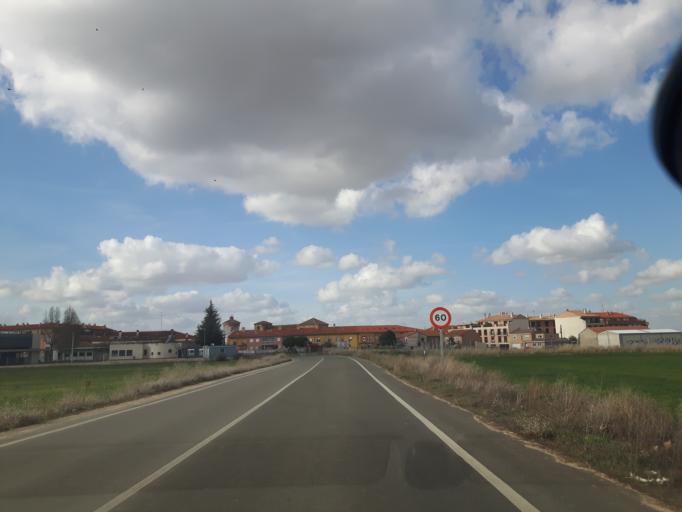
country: ES
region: Castille and Leon
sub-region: Provincia de Salamanca
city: Castellanos de Moriscos
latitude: 41.0160
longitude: -5.5881
